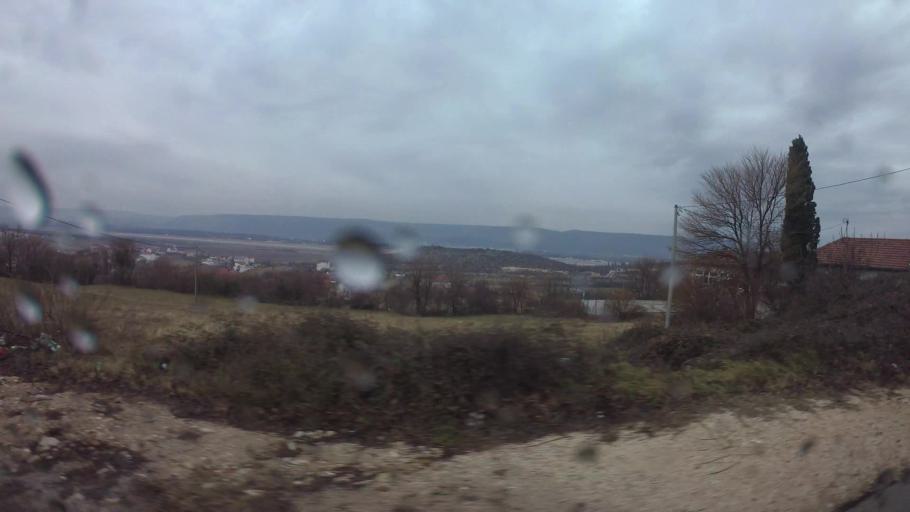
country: BA
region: Federation of Bosnia and Herzegovina
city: Blagaj
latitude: 43.2939
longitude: 17.8574
